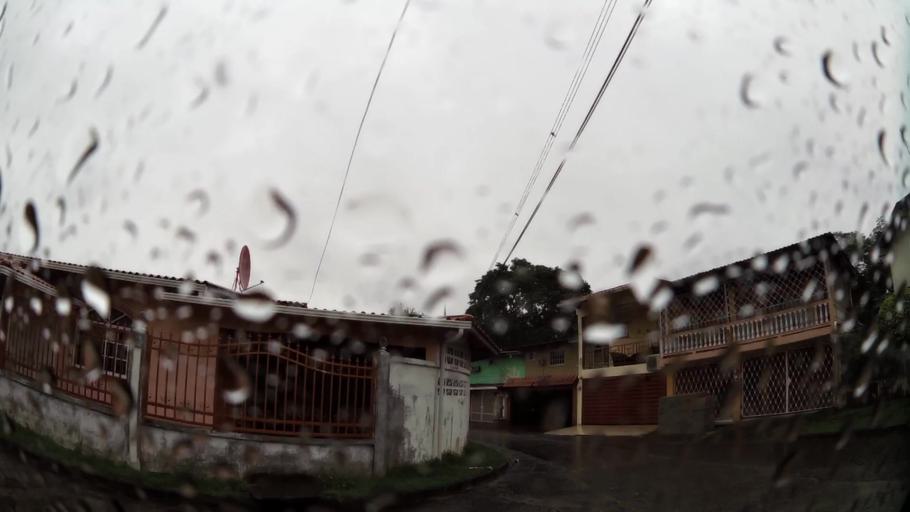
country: PA
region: Colon
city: Sabanitas
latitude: 9.3399
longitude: -79.8066
